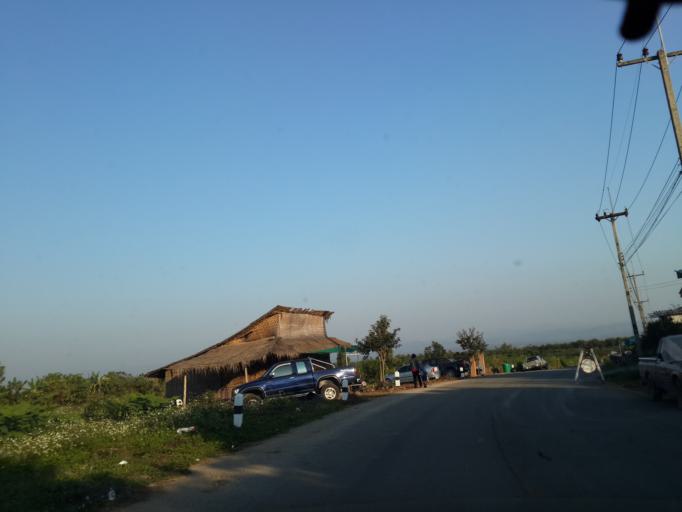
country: TH
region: Chiang Mai
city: Chai Prakan
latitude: 19.8161
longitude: 99.1106
